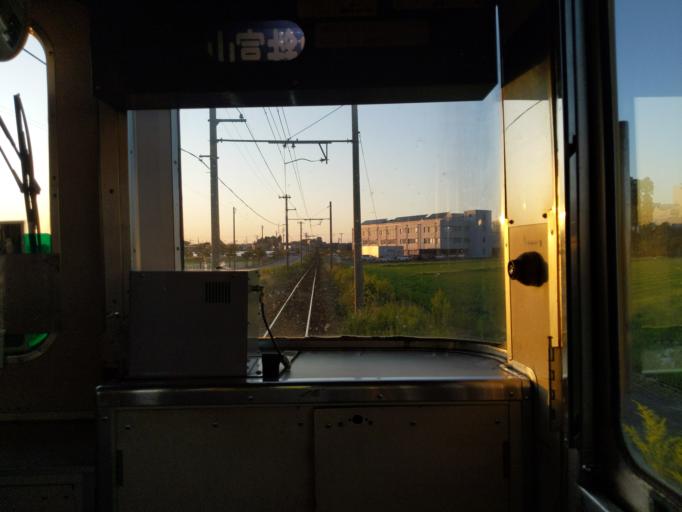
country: JP
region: Toyama
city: Kamiichi
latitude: 36.7025
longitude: 137.3128
